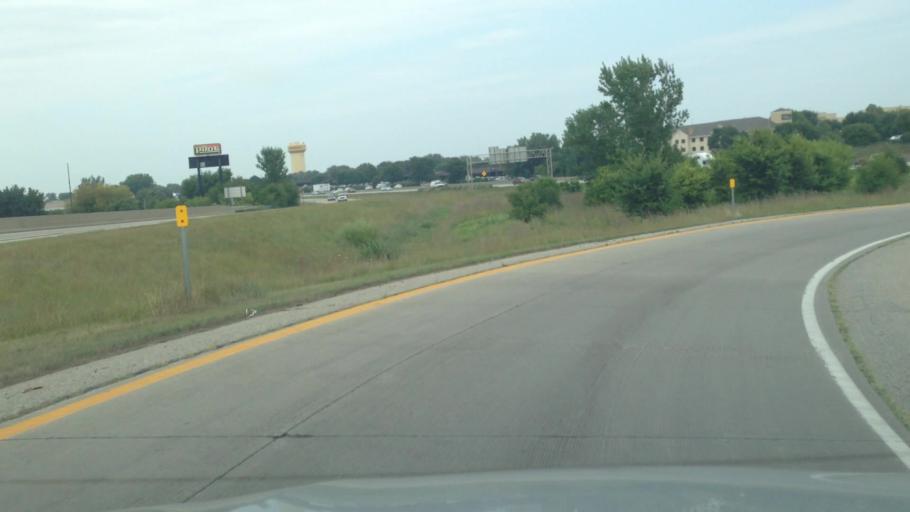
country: US
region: Iowa
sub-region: Polk County
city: Grimes
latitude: 41.6302
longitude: -93.7785
